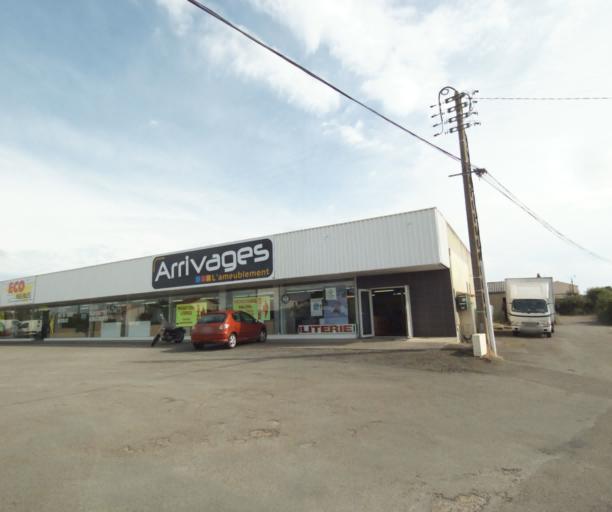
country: FR
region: Pays de la Loire
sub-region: Departement de la Vendee
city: Chateau-d'Olonne
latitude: 46.4822
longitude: -1.7192
